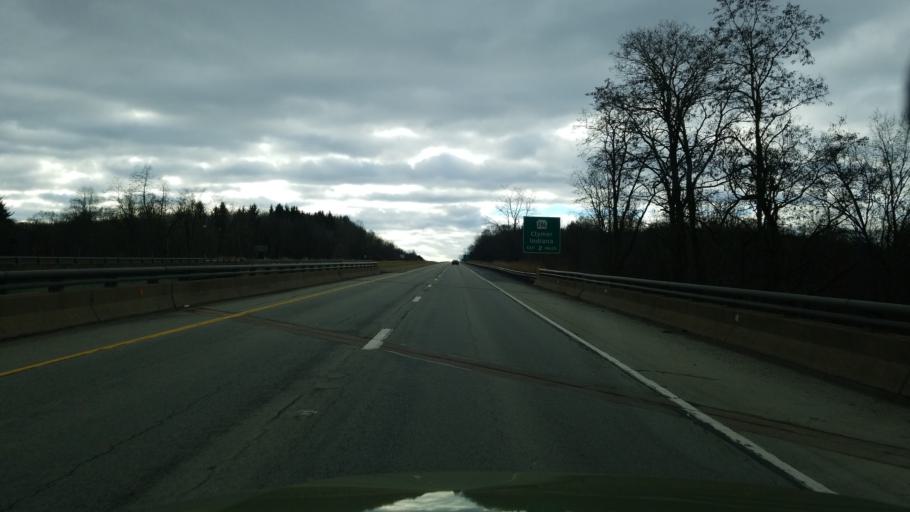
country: US
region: Pennsylvania
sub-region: Indiana County
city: Chevy Chase Heights
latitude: 40.6563
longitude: -79.1155
